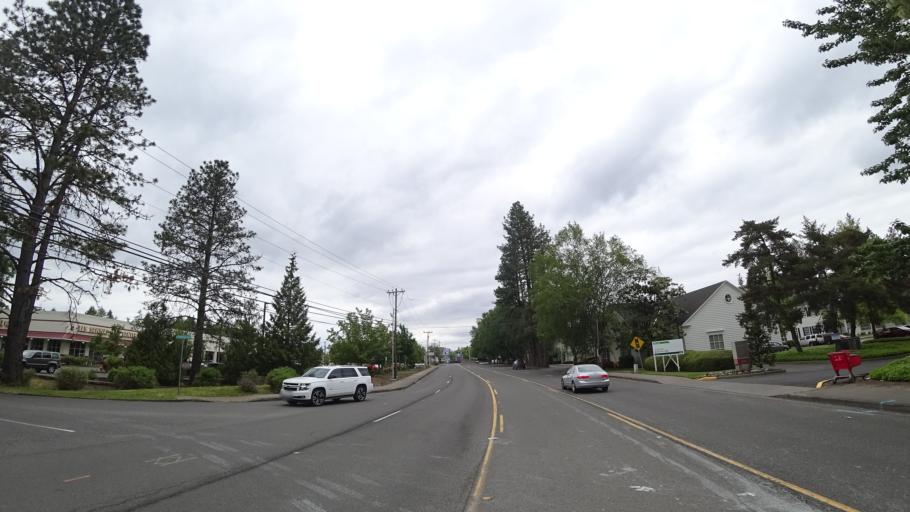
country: US
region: Oregon
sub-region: Washington County
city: Metzger
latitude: 45.4515
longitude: -122.7744
